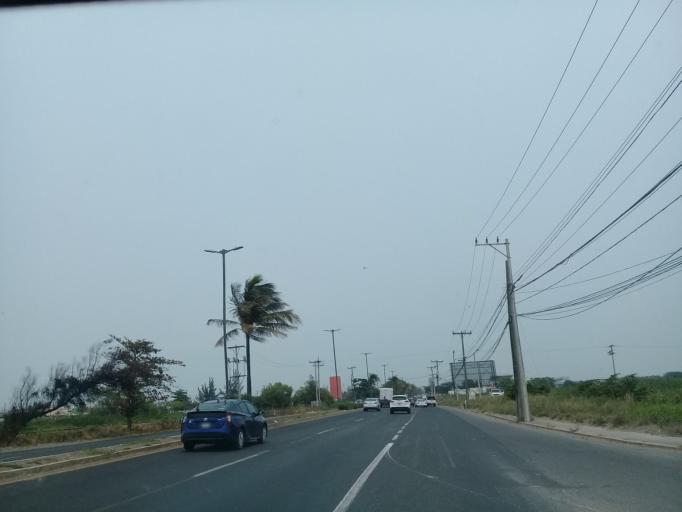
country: MX
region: Veracruz
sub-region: Veracruz
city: Hacienda Sotavento
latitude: 19.1491
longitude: -96.1723
